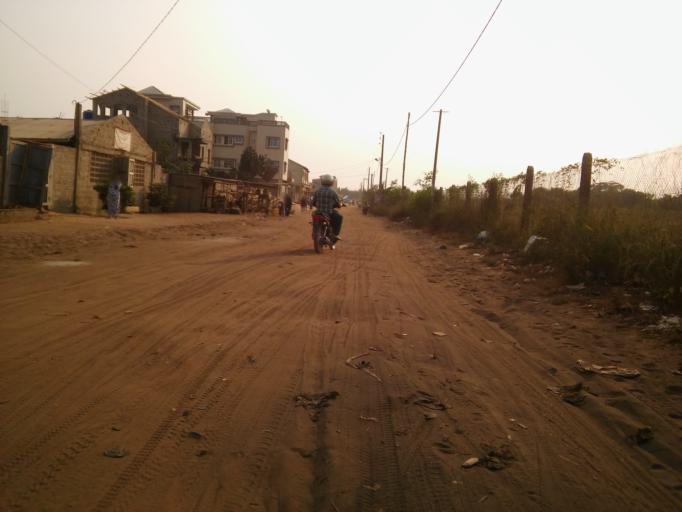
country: BJ
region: Atlantique
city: Abomey-Calavi
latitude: 6.4176
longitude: 2.3349
